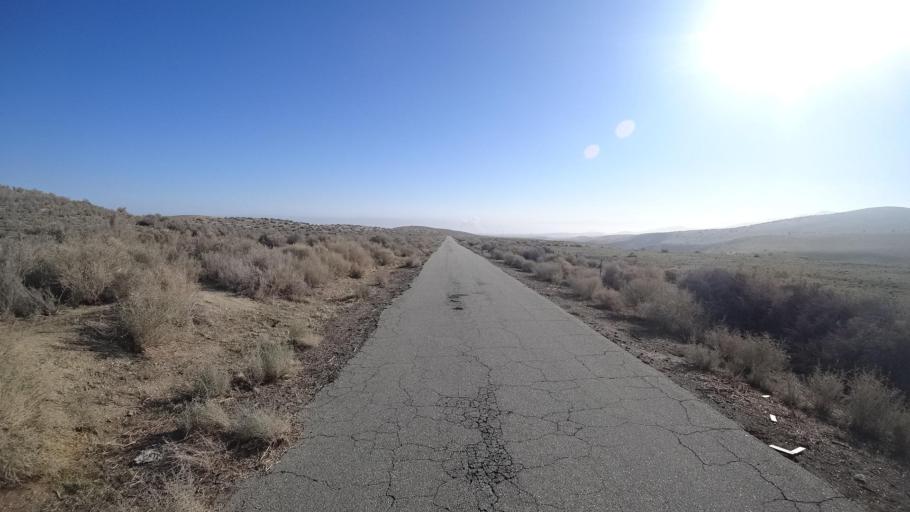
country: US
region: California
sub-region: Kern County
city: Taft Heights
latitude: 35.2319
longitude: -119.6515
